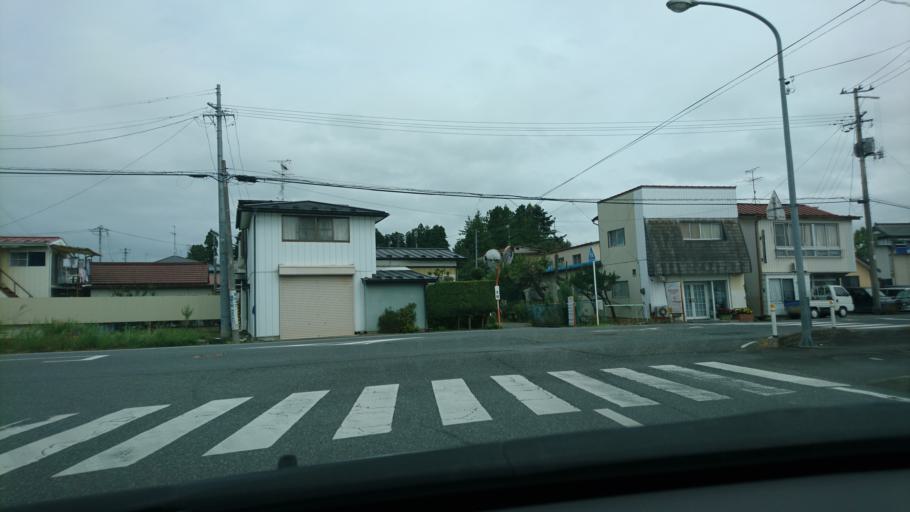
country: JP
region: Iwate
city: Ichinoseki
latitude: 38.7732
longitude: 141.1179
